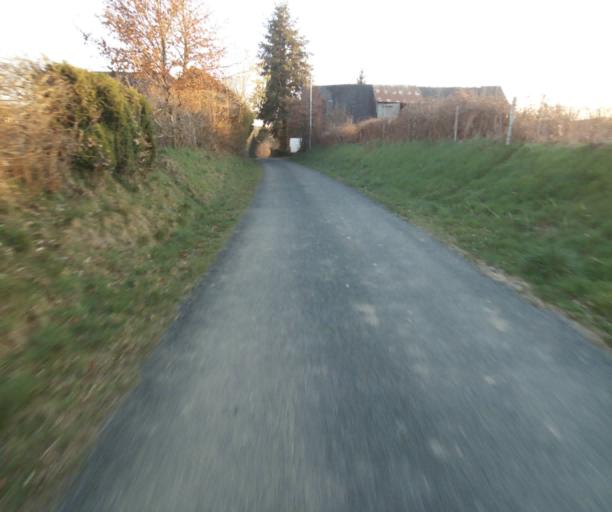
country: FR
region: Limousin
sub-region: Departement de la Correze
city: Saint-Clement
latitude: 45.3691
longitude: 1.6183
